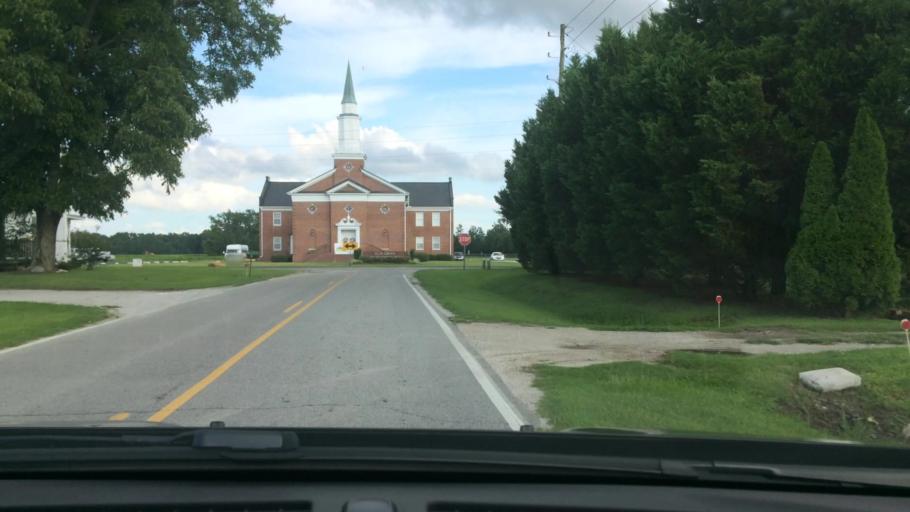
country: US
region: North Carolina
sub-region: Pitt County
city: Ayden
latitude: 35.4308
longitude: -77.4115
